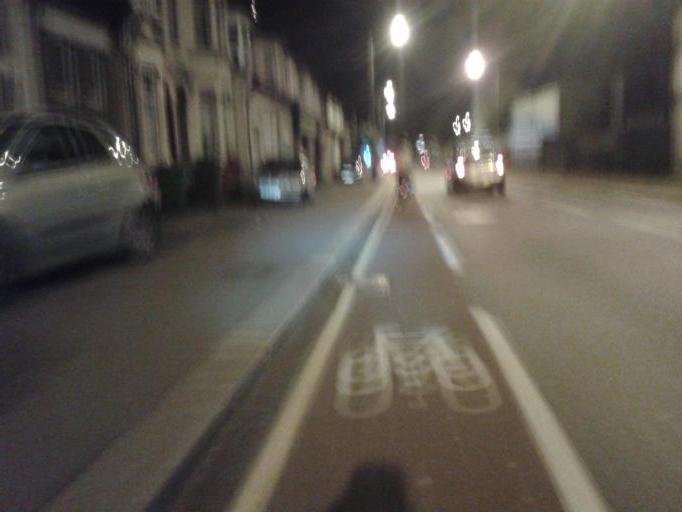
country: GB
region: England
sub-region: Greater London
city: Walthamstow
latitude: 51.5885
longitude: -0.0320
